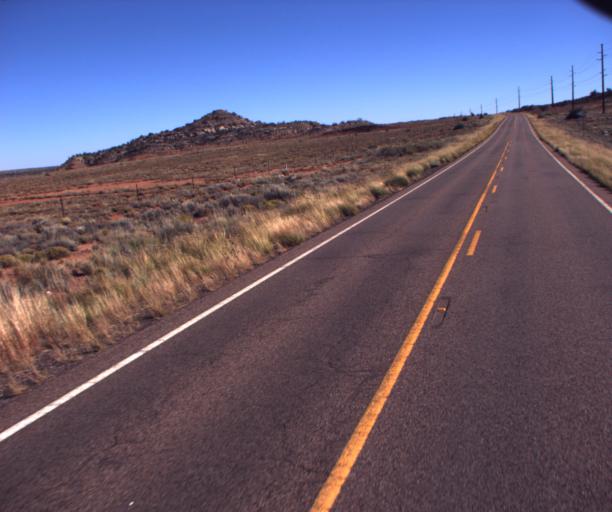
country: US
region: Arizona
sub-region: Navajo County
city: Taylor
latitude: 34.4938
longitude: -110.2131
